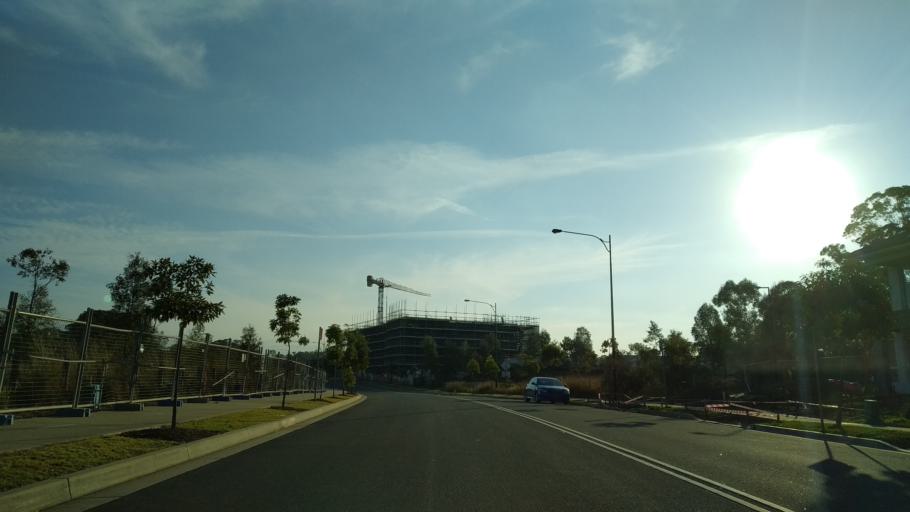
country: AU
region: New South Wales
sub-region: Penrith Municipality
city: Werrington Downs
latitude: -33.7284
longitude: 150.7307
